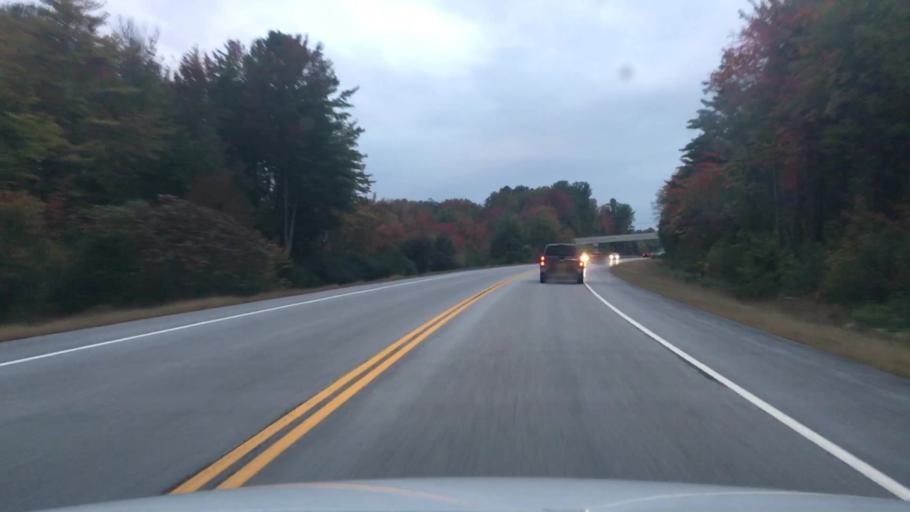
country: US
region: Maine
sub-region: Cumberland County
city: Gorham
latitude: 43.6724
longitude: -70.4619
